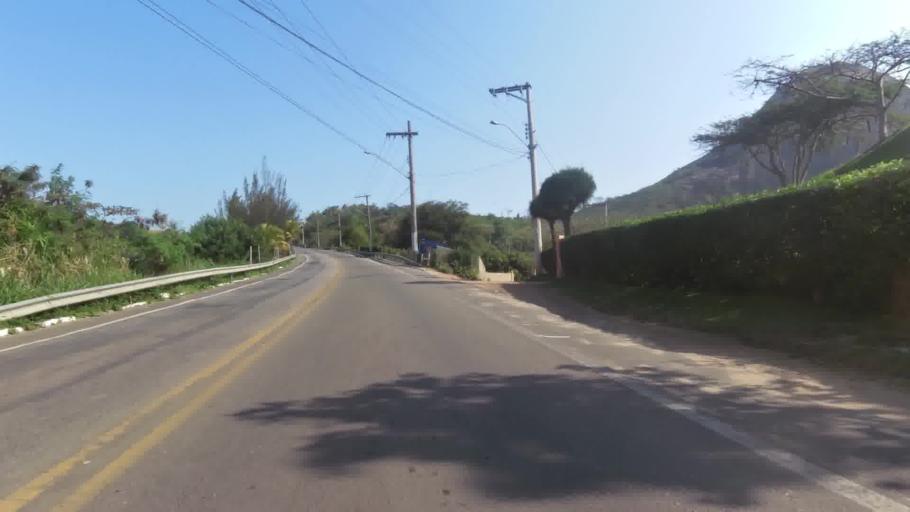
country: BR
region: Espirito Santo
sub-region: Piuma
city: Piuma
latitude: -20.8647
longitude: -40.7601
